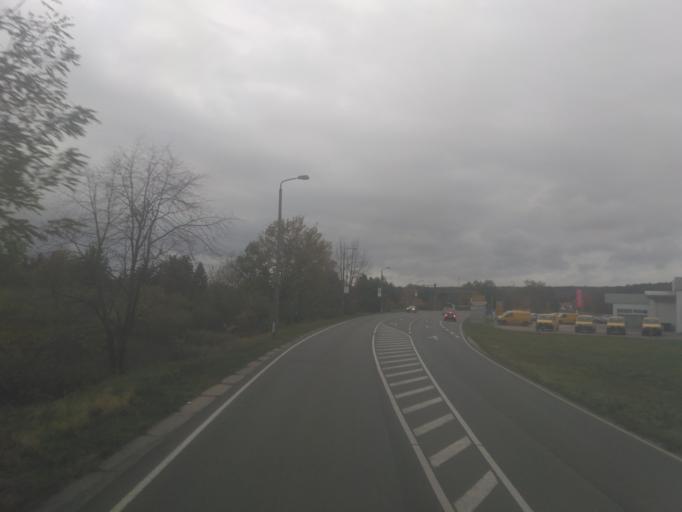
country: DE
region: Brandenburg
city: Elsterwerda
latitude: 51.4674
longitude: 13.4957
